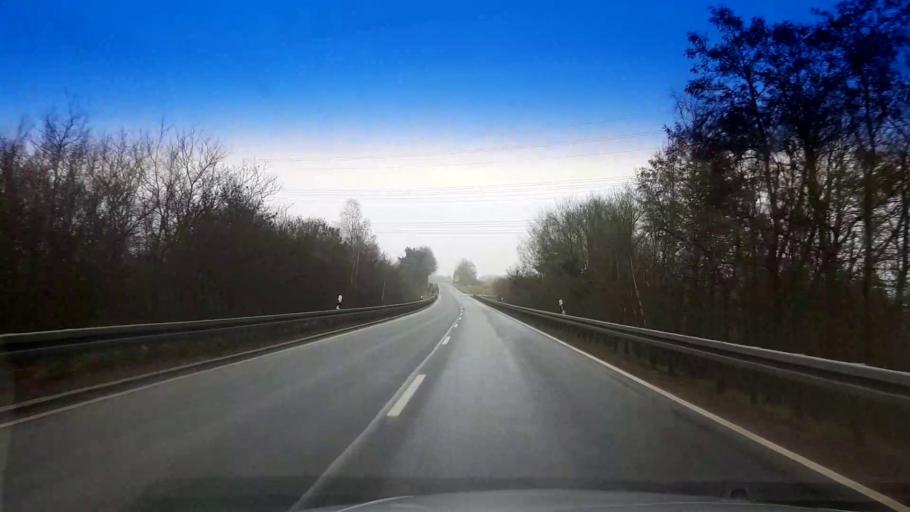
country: DE
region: Bavaria
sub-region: Upper Palatinate
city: Wiesau
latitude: 49.8605
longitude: 12.2104
